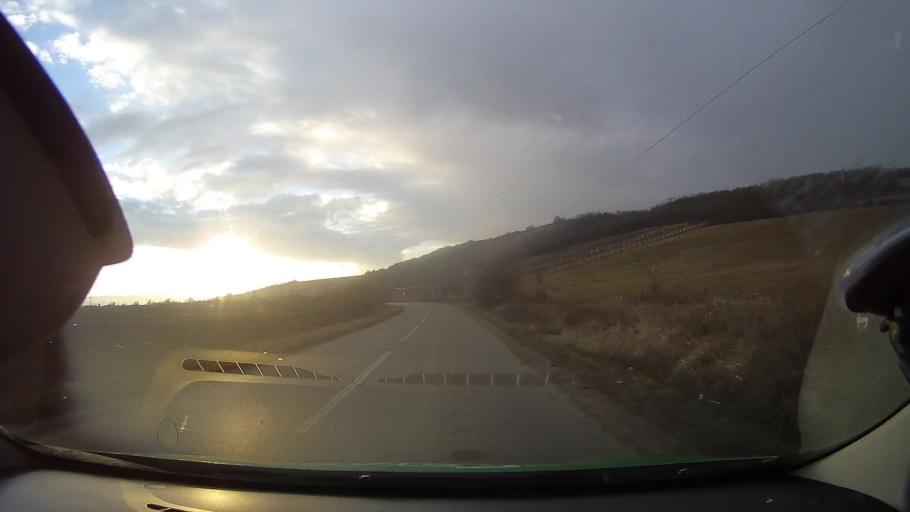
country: RO
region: Alba
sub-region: Oras Ocna Mures
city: Razboieni-Cetate
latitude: 46.4239
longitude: 23.8828
